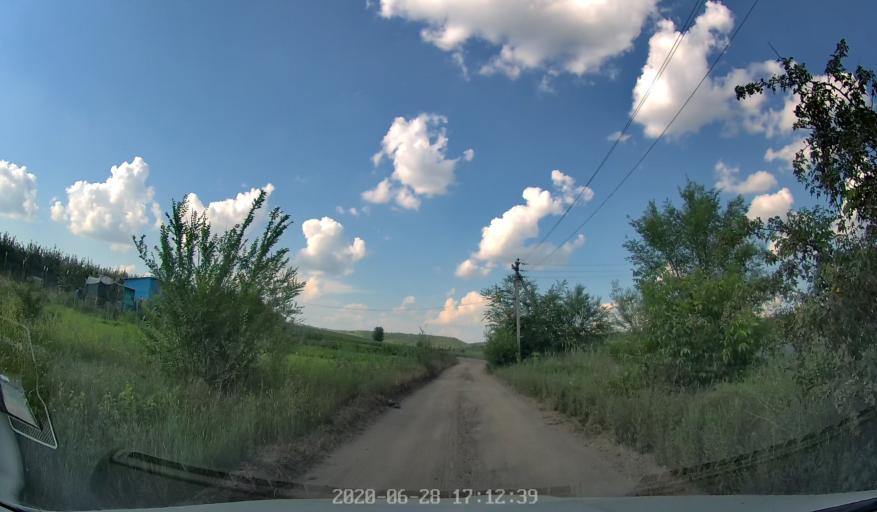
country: MD
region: Chisinau
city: Vatra
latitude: 46.9892
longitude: 28.6981
